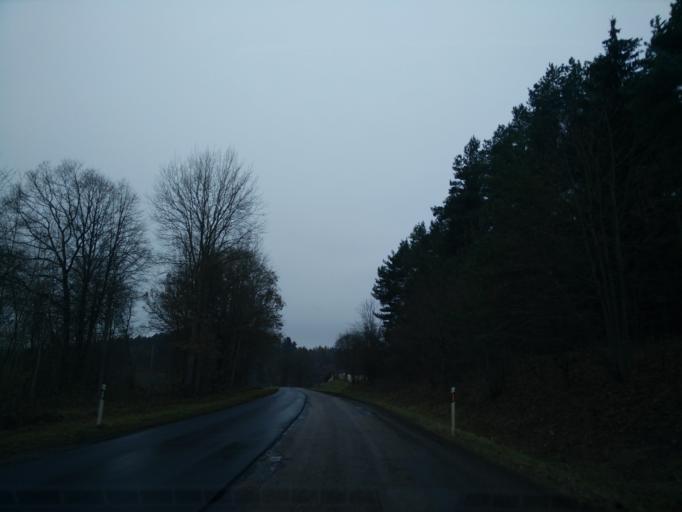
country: LT
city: Ariogala
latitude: 55.2961
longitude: 23.4414
